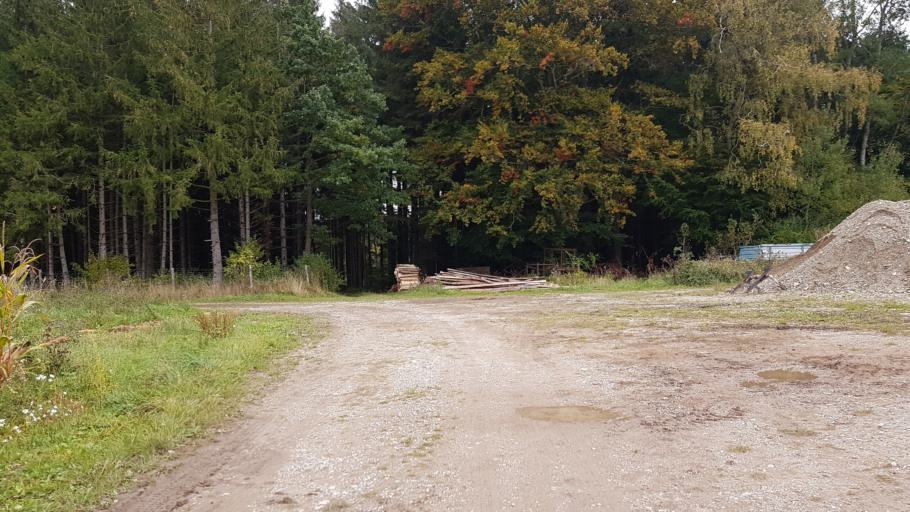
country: DE
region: Bavaria
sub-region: Upper Bavaria
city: Gilching
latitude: 48.1016
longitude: 11.3392
